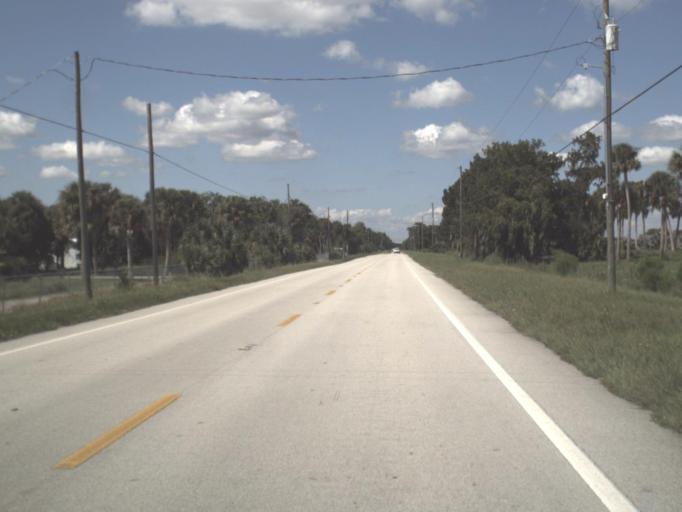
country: US
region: Florida
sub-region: Okeechobee County
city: Taylor Creek
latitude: 27.1663
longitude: -80.7183
